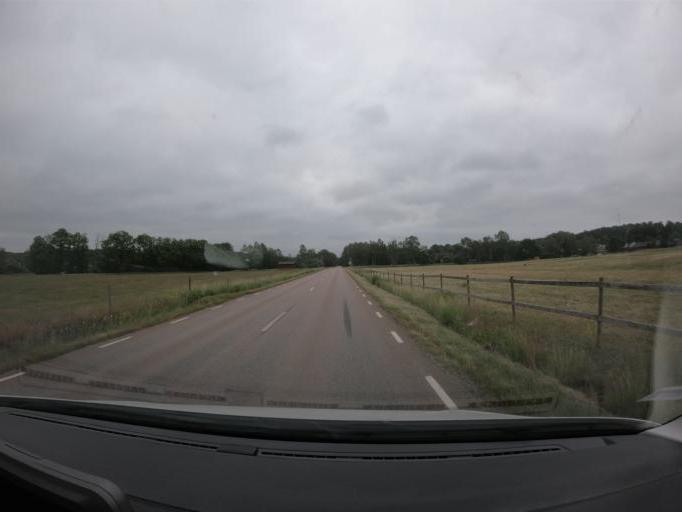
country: SE
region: Skane
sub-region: Klippans Kommun
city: Ljungbyhed
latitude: 56.1368
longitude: 13.2850
